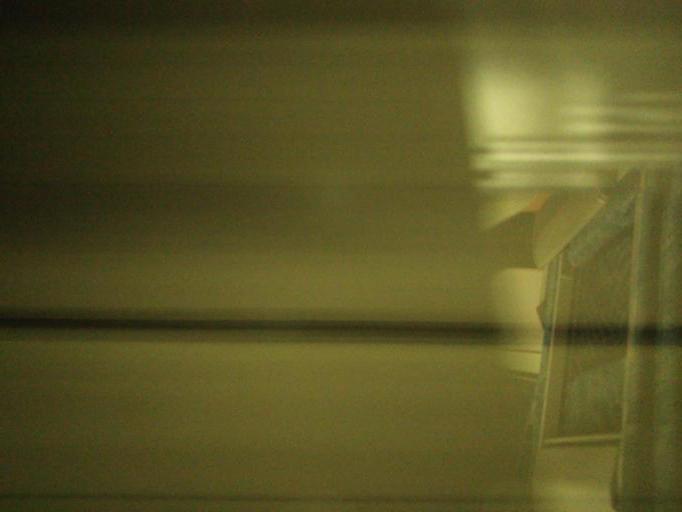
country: JP
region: Kochi
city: Nakamura
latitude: 33.0675
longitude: 133.1068
